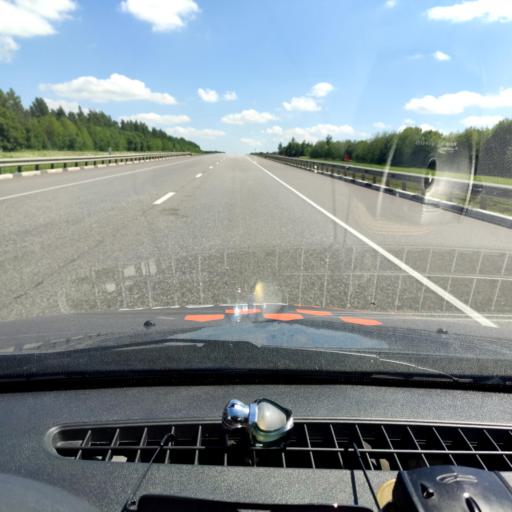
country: RU
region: Orjol
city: Zmiyevka
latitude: 52.8156
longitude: 36.2852
